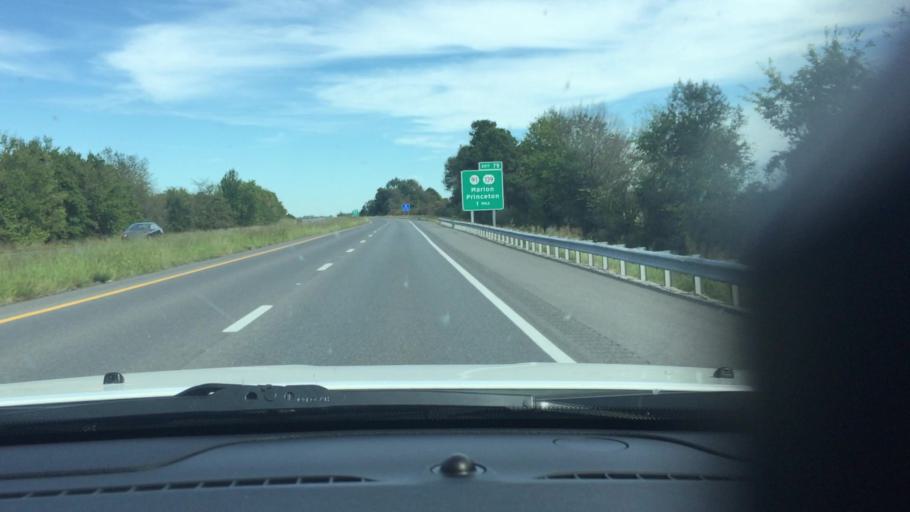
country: US
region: Kentucky
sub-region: Caldwell County
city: Princeton
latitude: 37.1181
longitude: -87.9157
